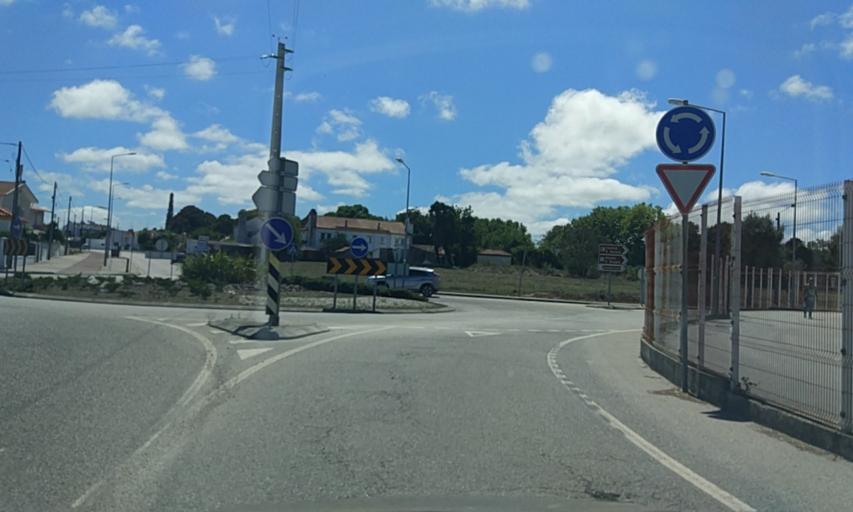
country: PT
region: Aveiro
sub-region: Ilhavo
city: Ilhavo
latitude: 40.5911
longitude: -8.6816
